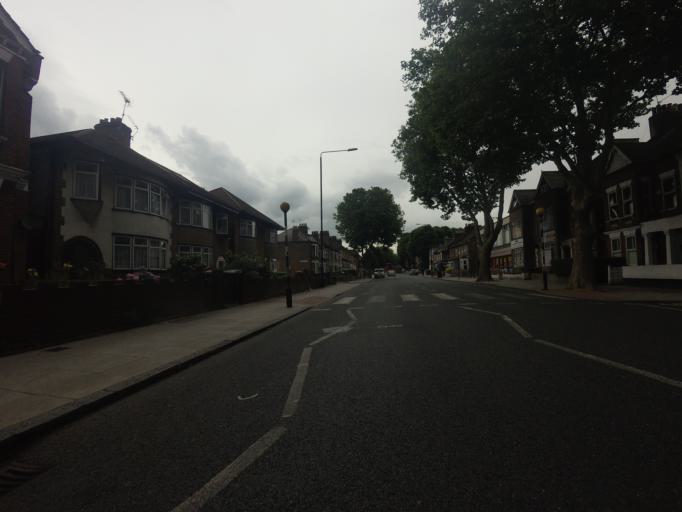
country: GB
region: England
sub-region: Greater London
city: East Ham
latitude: 51.5237
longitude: 0.0255
